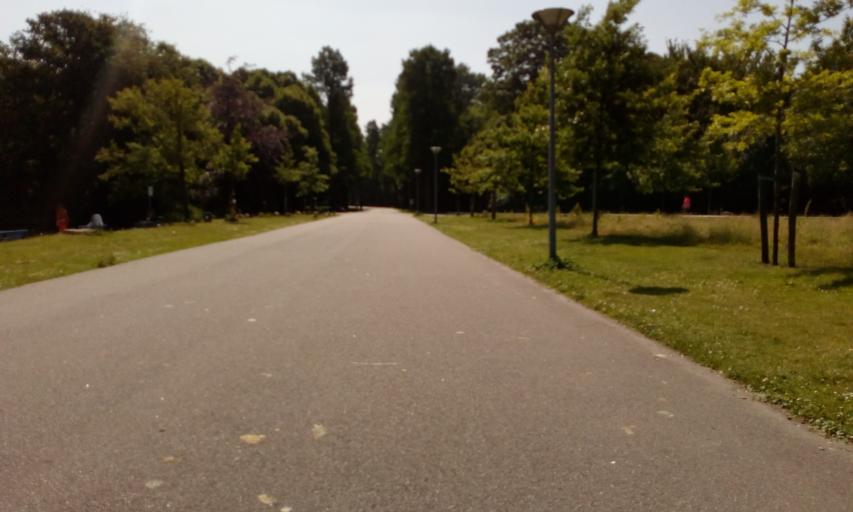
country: NL
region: South Holland
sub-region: Gemeente Den Haag
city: The Hague
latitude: 52.0543
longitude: 4.2815
